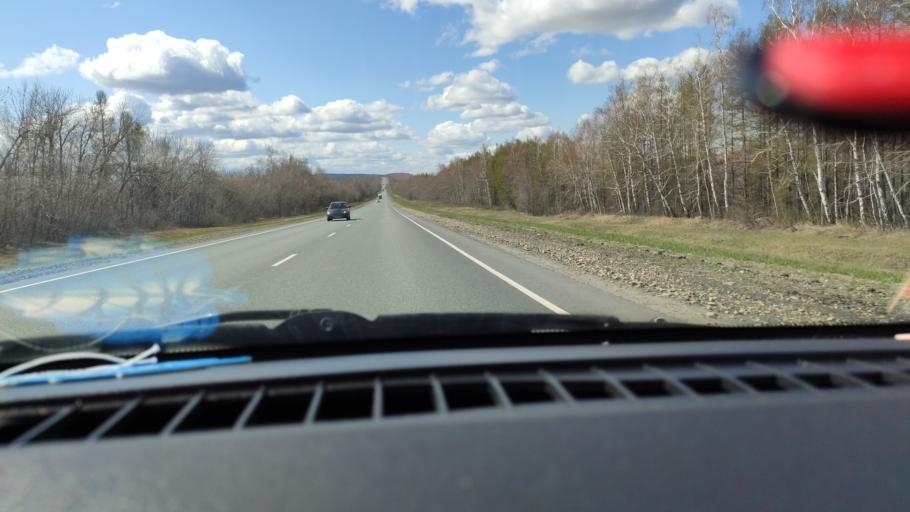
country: RU
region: Saratov
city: Khvalynsk
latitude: 52.5795
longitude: 48.1146
